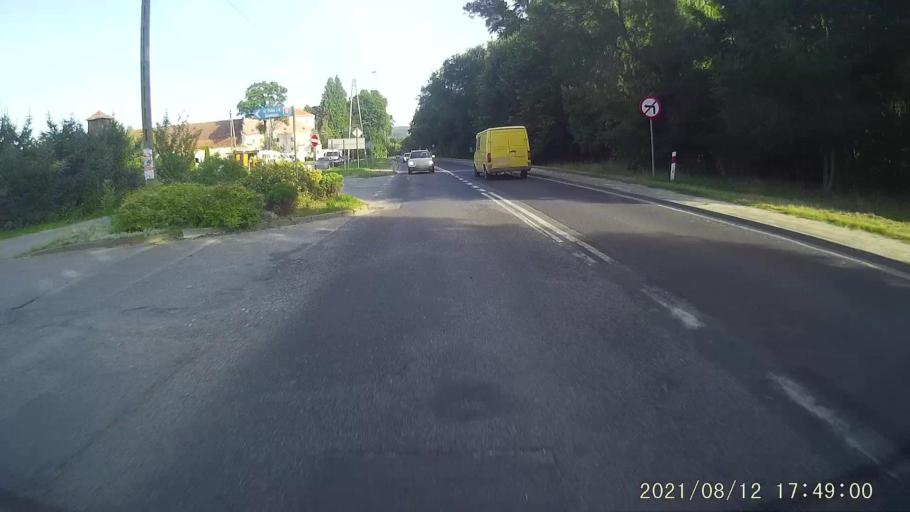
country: PL
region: Lower Silesian Voivodeship
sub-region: Powiat klodzki
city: Klodzko
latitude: 50.3586
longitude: 16.7229
